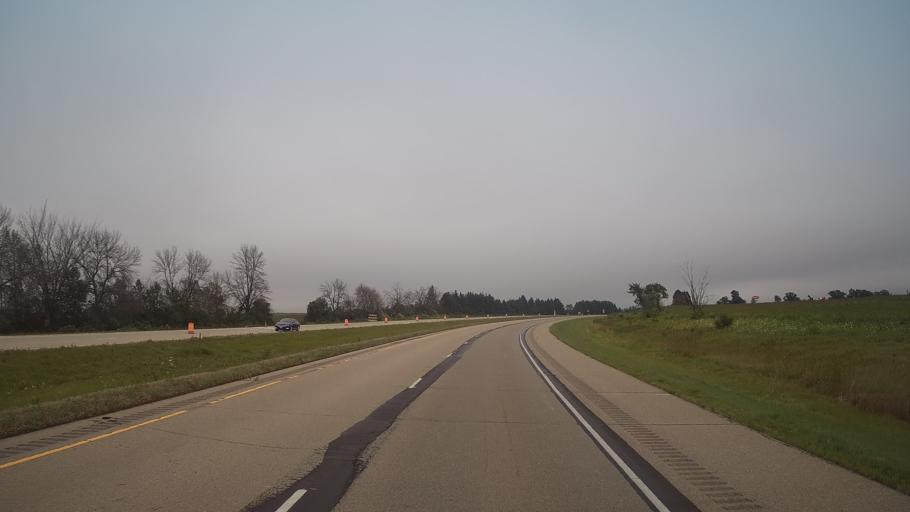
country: US
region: Minnesota
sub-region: Olmsted County
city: Stewartville
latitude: 43.8785
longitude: -92.5057
